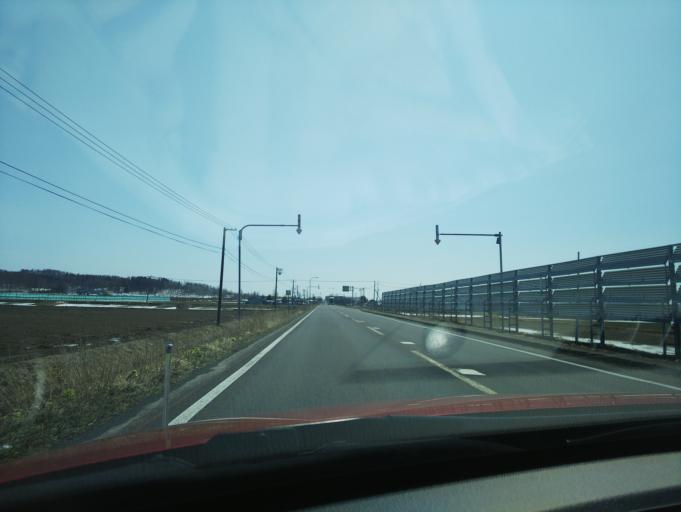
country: JP
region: Hokkaido
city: Nayoro
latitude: 44.2672
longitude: 142.3947
